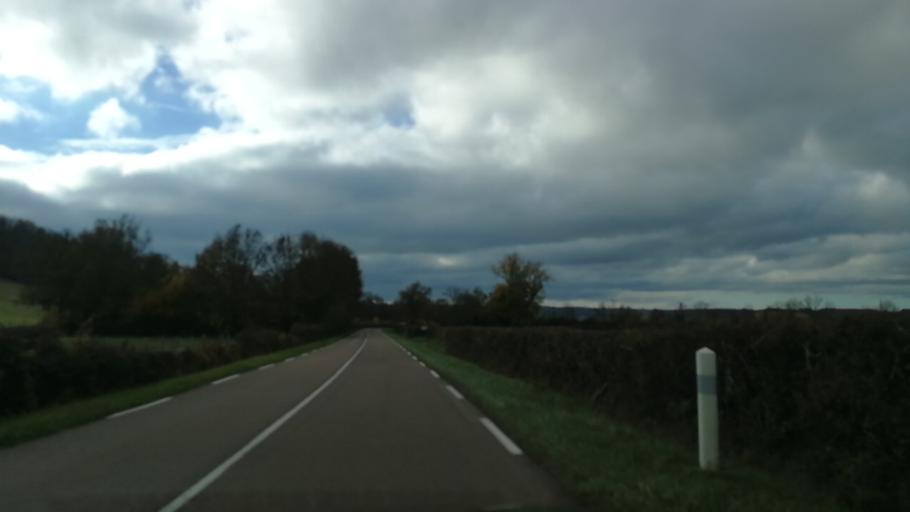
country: FR
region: Bourgogne
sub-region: Departement de la Cote-d'Or
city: Pouilly-en-Auxois
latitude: 47.2701
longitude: 4.4084
